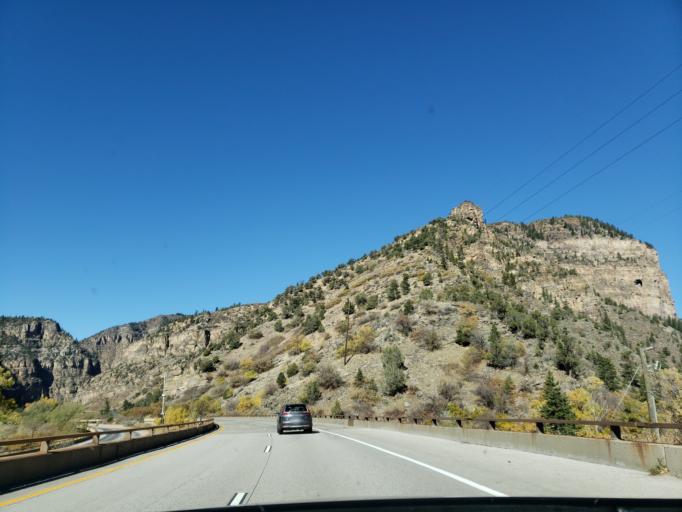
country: US
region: Colorado
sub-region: Garfield County
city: Glenwood Springs
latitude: 39.5607
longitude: -107.2491
